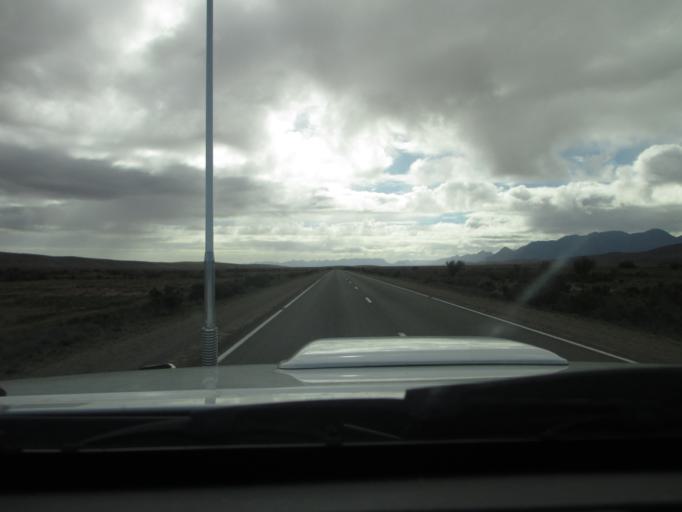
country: AU
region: South Australia
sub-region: Flinders Ranges
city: Quorn
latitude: -31.6149
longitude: 138.3961
